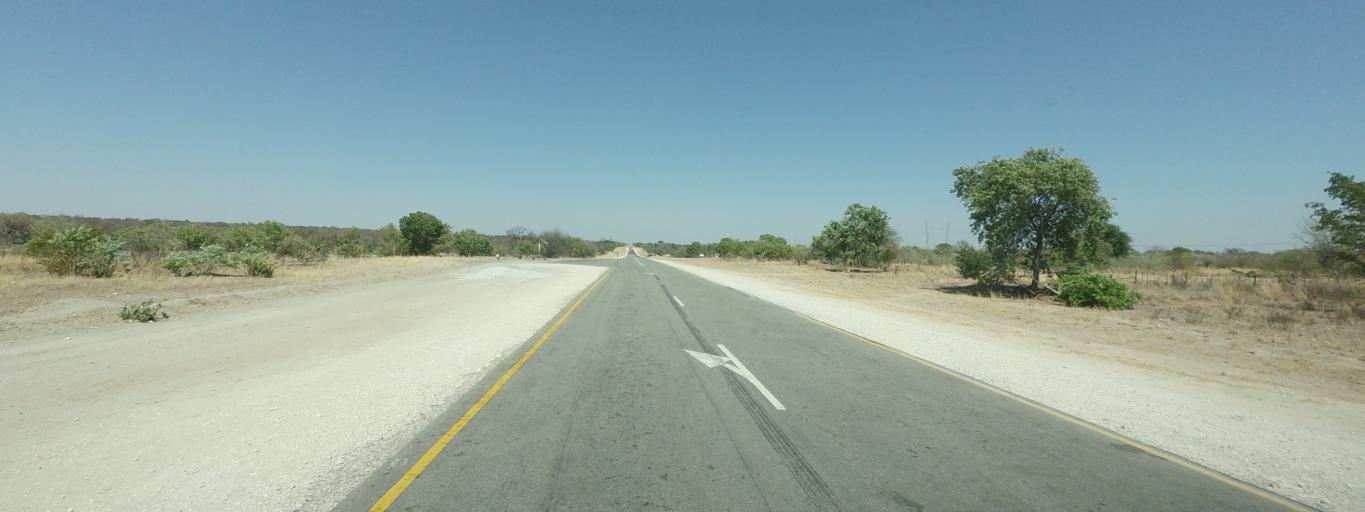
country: BW
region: North West
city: Shakawe
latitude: -17.9570
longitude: 22.5615
